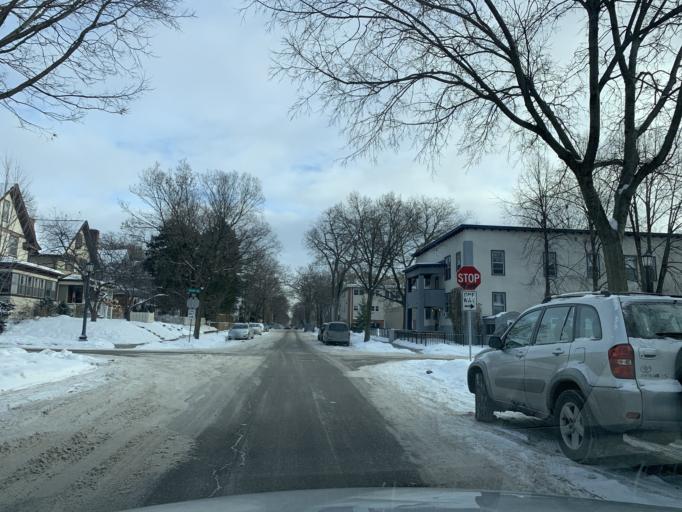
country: US
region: Minnesota
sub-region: Hennepin County
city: Minneapolis
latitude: 44.9573
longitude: -93.2846
